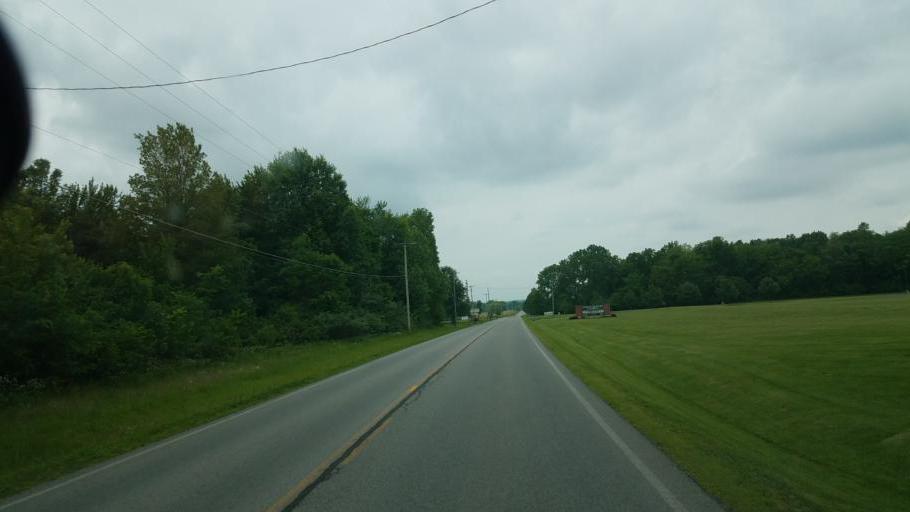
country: US
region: Ohio
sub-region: Delaware County
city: Delaware
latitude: 40.3205
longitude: -83.1364
